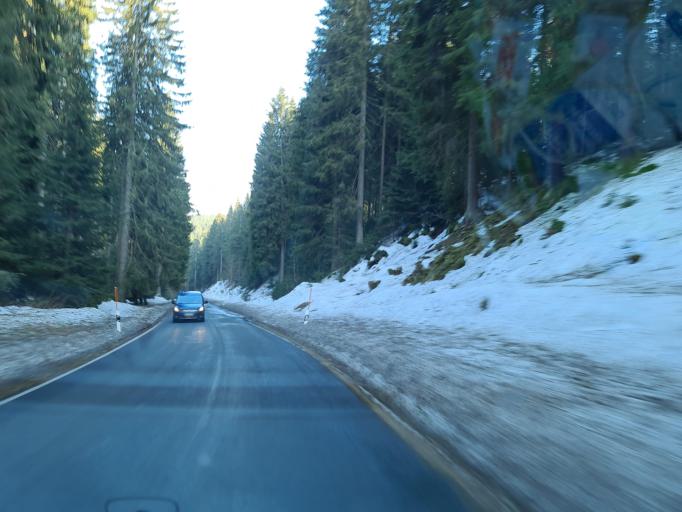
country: DE
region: Saxony
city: Eibenstock
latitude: 50.4395
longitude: 12.6140
